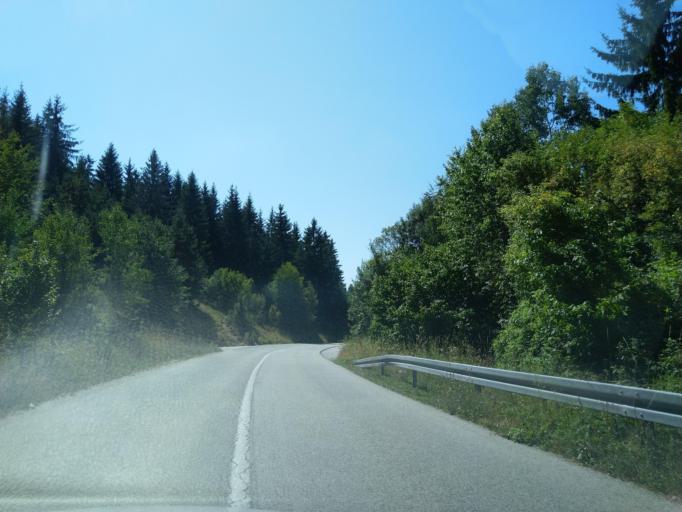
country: RS
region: Central Serbia
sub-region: Zlatiborski Okrug
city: Nova Varos
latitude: 43.3504
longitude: 19.8533
